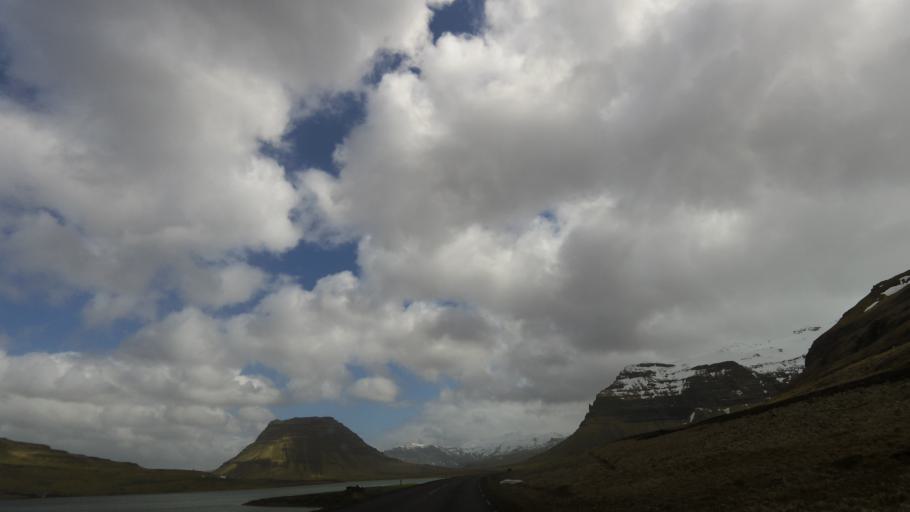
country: IS
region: West
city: Olafsvik
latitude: 64.9440
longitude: -23.3912
